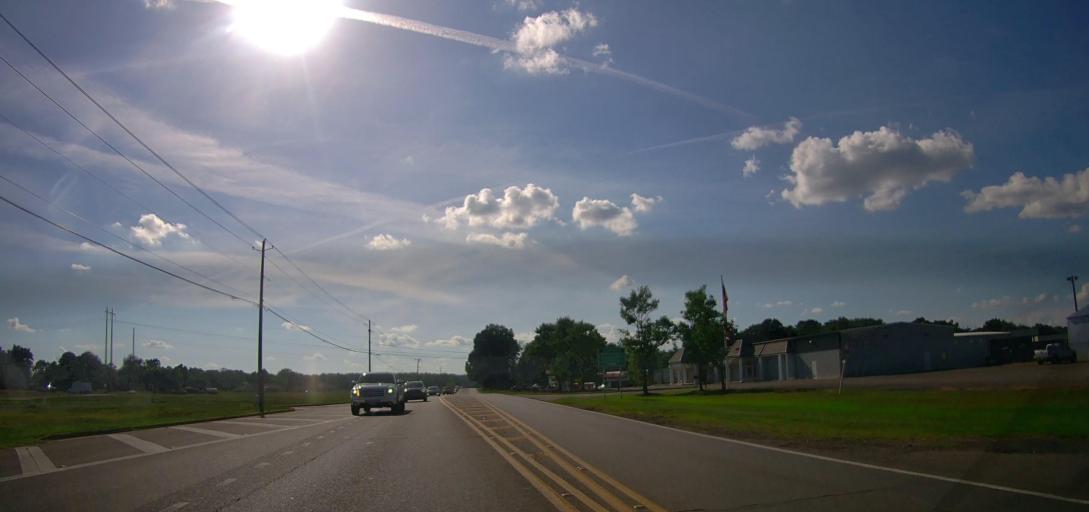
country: US
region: Alabama
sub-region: Tuscaloosa County
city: Holt
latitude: 33.1899
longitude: -87.4593
